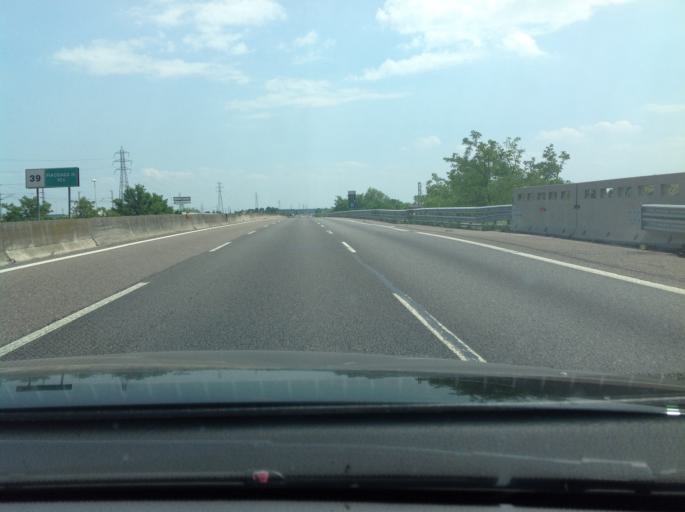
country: IT
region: Lombardy
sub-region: Provincia di Lodi
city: Ospedaletto Lodigiano
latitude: 45.1715
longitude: 9.5927
